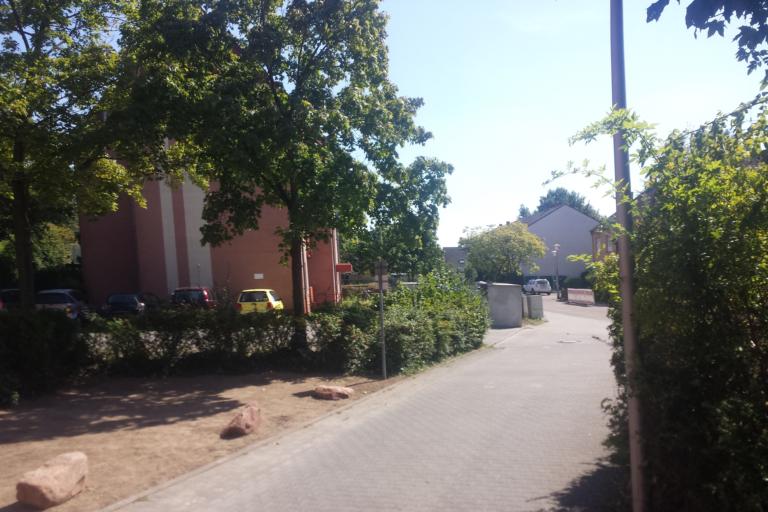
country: DE
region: Baden-Wuerttemberg
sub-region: Karlsruhe Region
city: Mannheim
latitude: 49.5261
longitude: 8.5063
